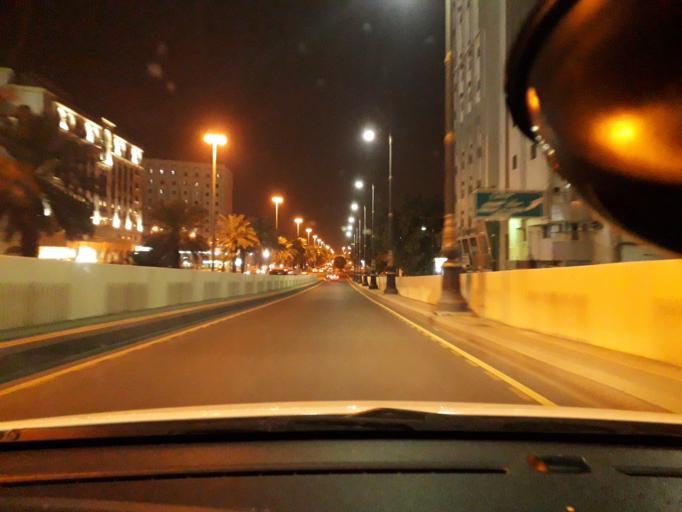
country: SA
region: Al Madinah al Munawwarah
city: Medina
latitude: 24.4673
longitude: 39.6000
